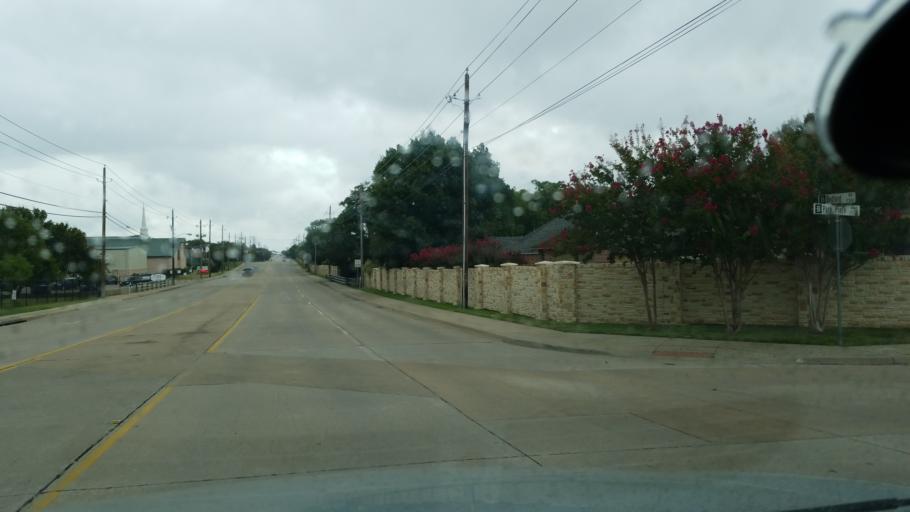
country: US
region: Texas
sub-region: Tarrant County
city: Bedford
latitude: 32.8447
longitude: -97.1292
